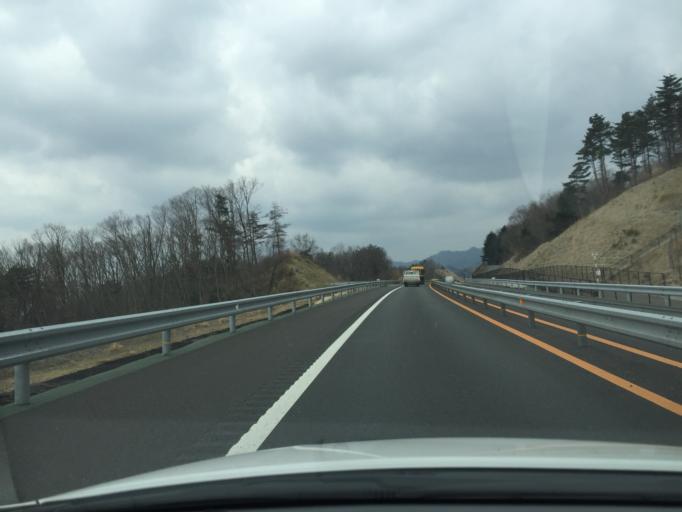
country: JP
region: Miyagi
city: Marumori
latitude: 37.8336
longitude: 140.8785
